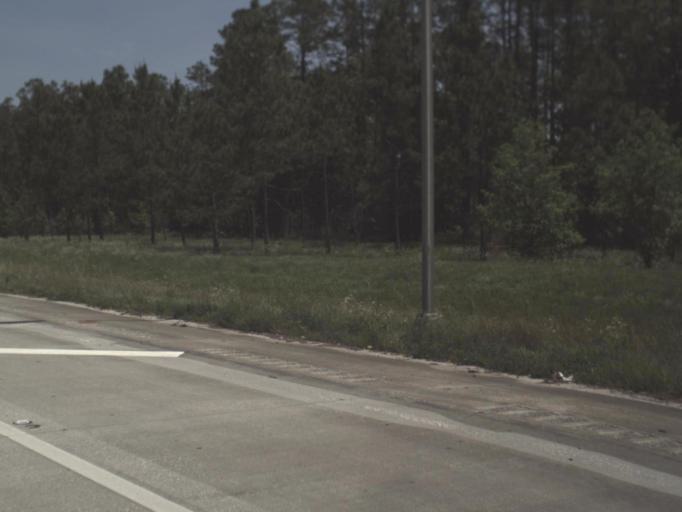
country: US
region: Florida
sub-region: Saint Johns County
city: Palm Valley
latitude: 30.1936
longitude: -81.5135
